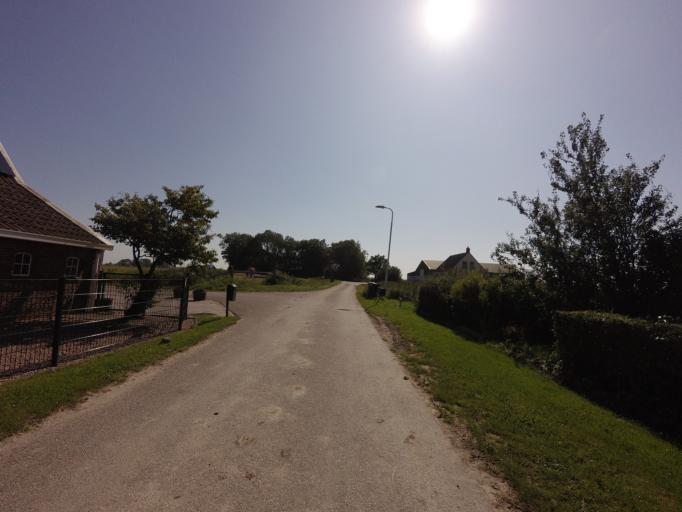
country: NL
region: Friesland
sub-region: Gemeente Dongeradeel
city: Holwerd
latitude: 53.3672
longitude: 5.9235
